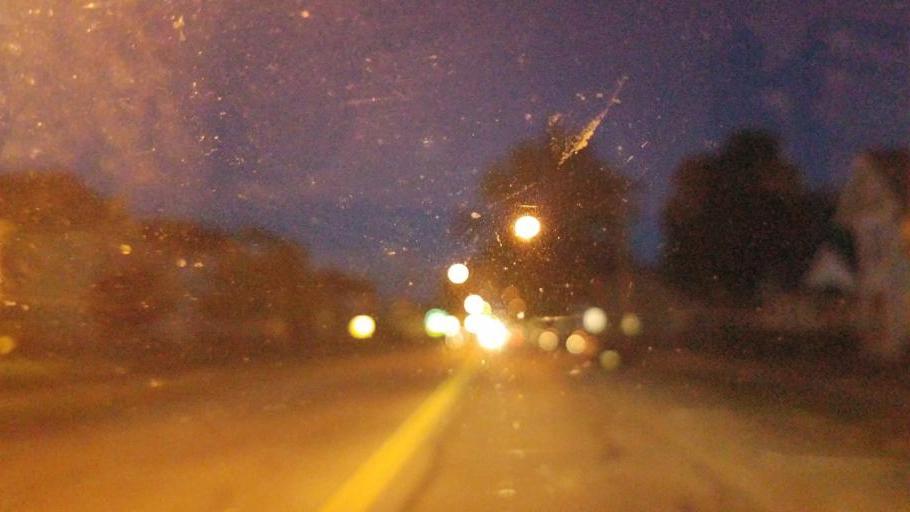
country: US
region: Ohio
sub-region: Highland County
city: Greenfield
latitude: 39.3507
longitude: -83.3869
